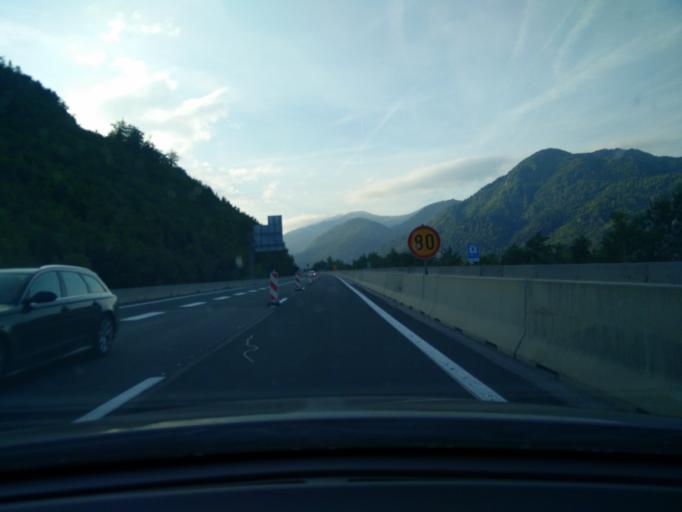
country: SI
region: Jesenice
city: Slovenski Javornik
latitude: 46.4175
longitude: 14.0899
